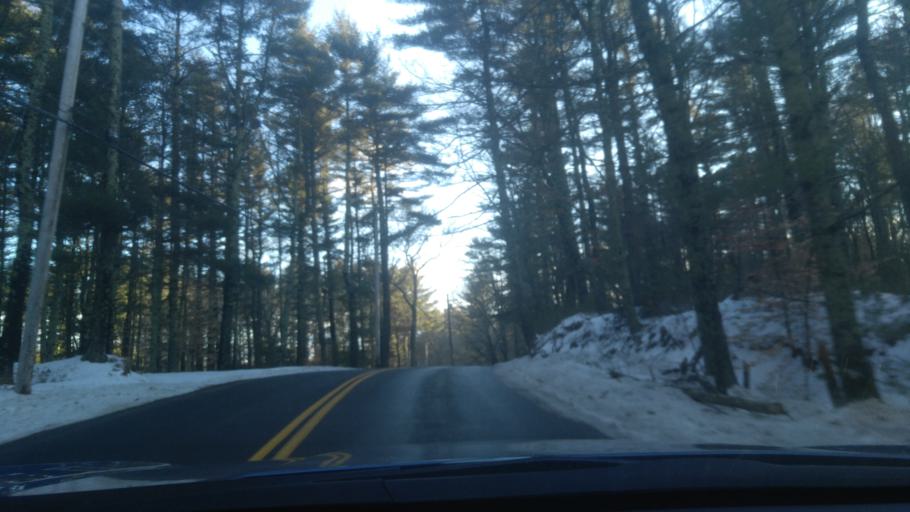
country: US
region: Rhode Island
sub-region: Kent County
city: Coventry
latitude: 41.7177
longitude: -71.6529
